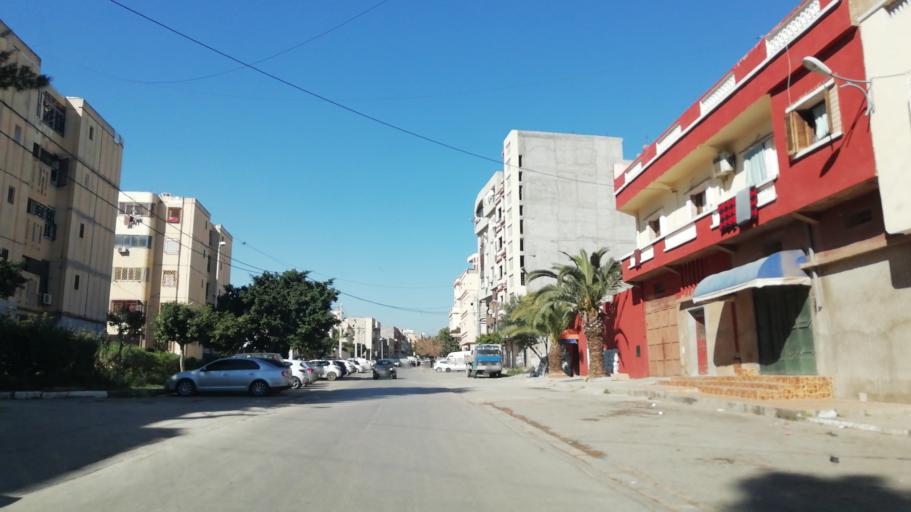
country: DZ
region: Oran
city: Oran
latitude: 35.6888
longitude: -0.6128
